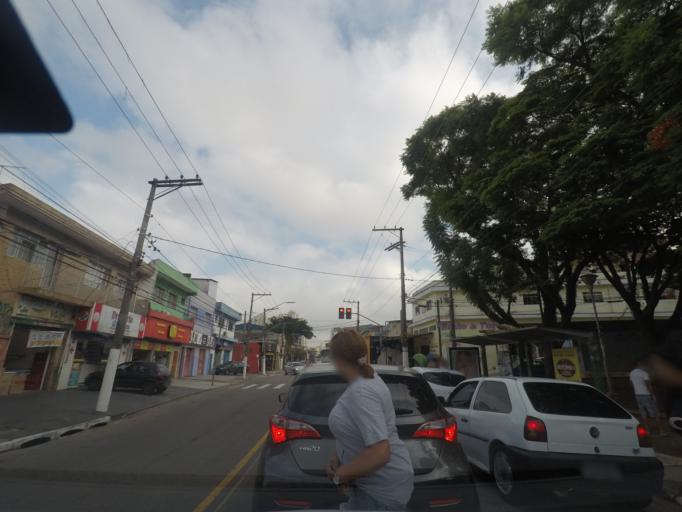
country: BR
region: Sao Paulo
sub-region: Osasco
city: Osasco
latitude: -23.5629
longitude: -46.7817
